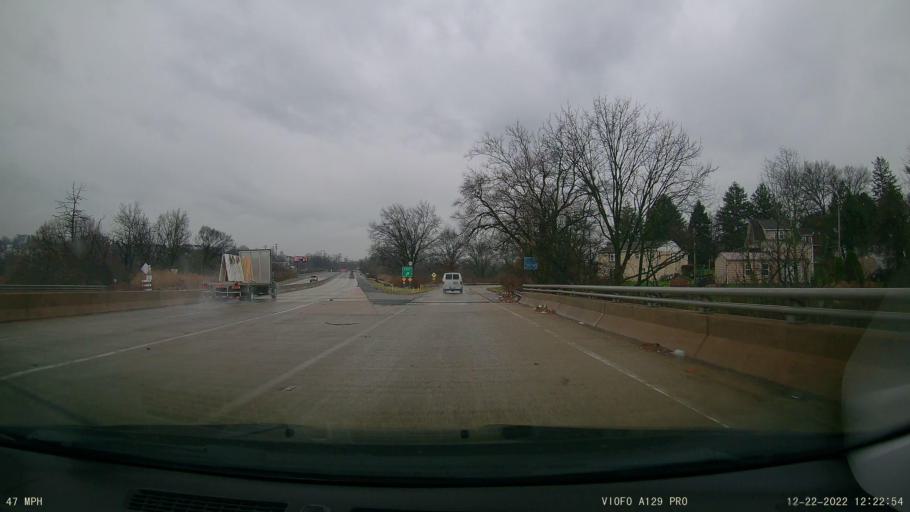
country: US
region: Pennsylvania
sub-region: Montgomery County
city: Bridgeport
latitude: 40.1078
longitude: -75.3513
